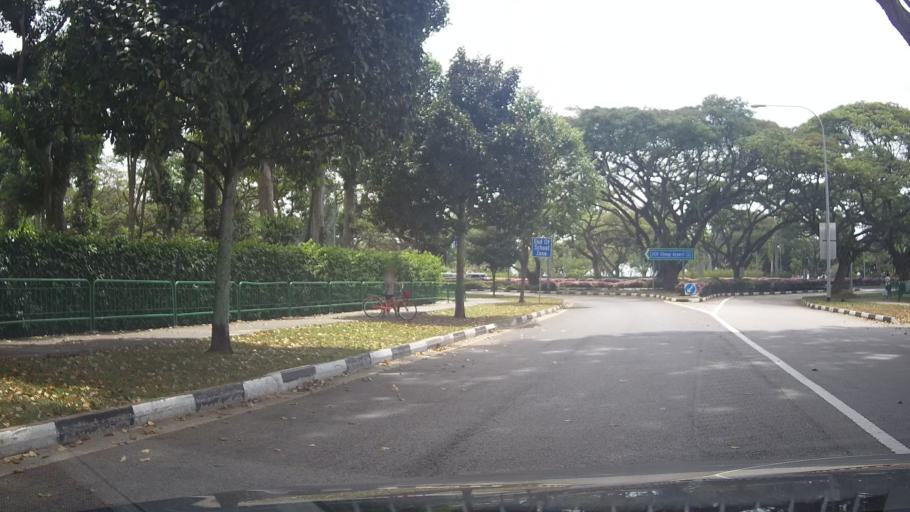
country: SG
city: Singapore
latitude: 1.3056
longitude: 103.9210
